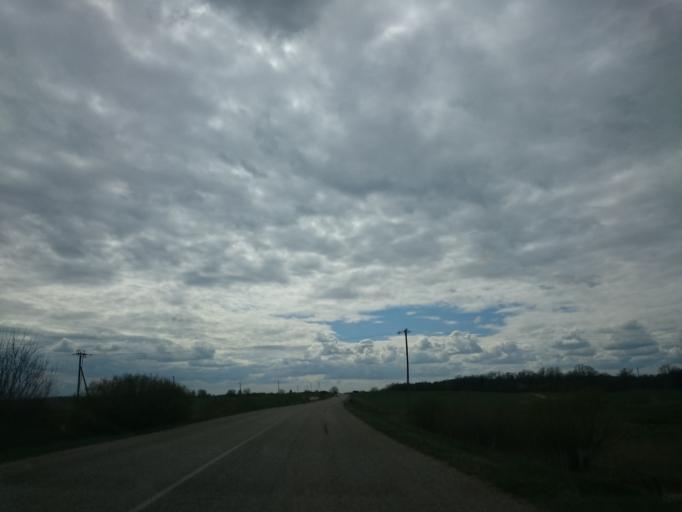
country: LV
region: Aizpute
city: Aizpute
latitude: 56.7746
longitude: 21.6324
